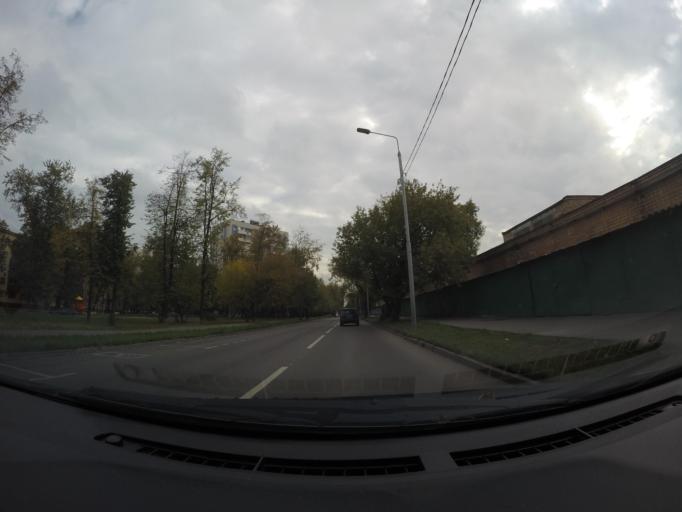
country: RU
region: Moscow
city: Lefortovo
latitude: 55.7659
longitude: 37.7269
